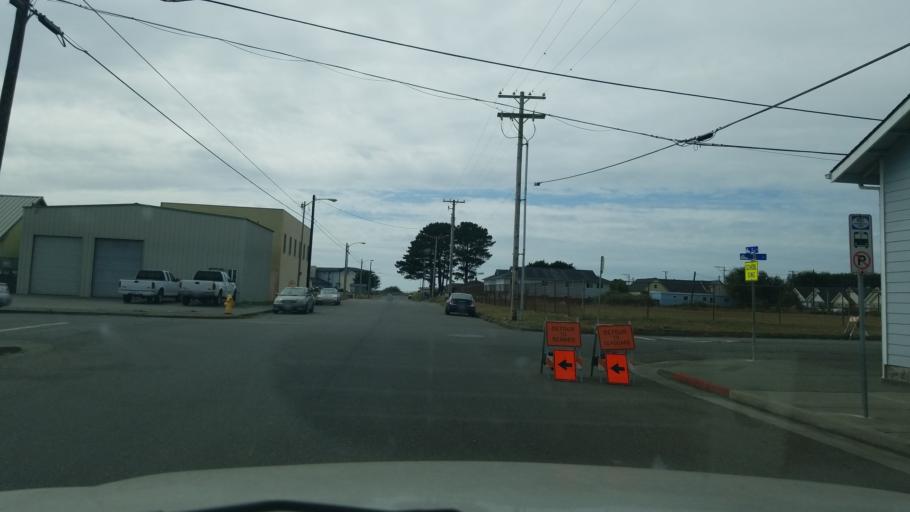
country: US
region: California
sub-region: Del Norte County
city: Crescent City
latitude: 41.7498
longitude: -124.2006
